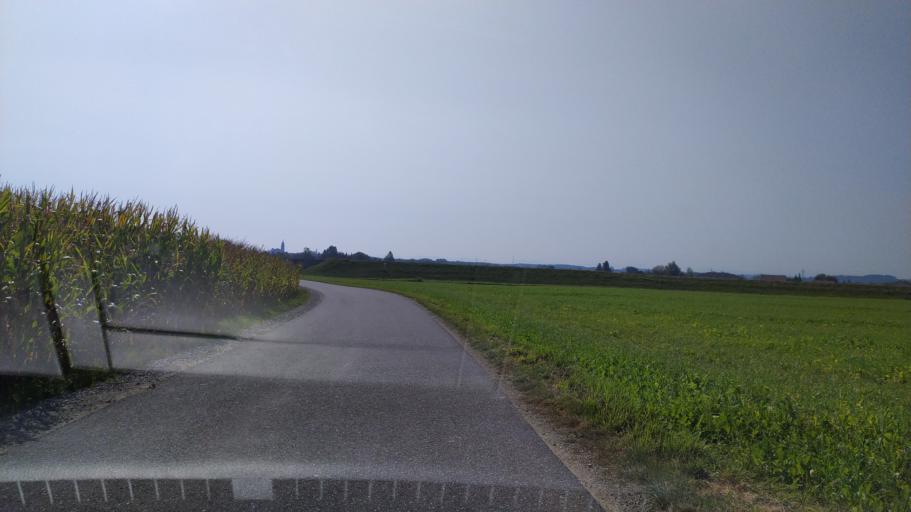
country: AT
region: Lower Austria
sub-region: Politischer Bezirk Amstetten
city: Strengberg
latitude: 48.1916
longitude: 14.7062
